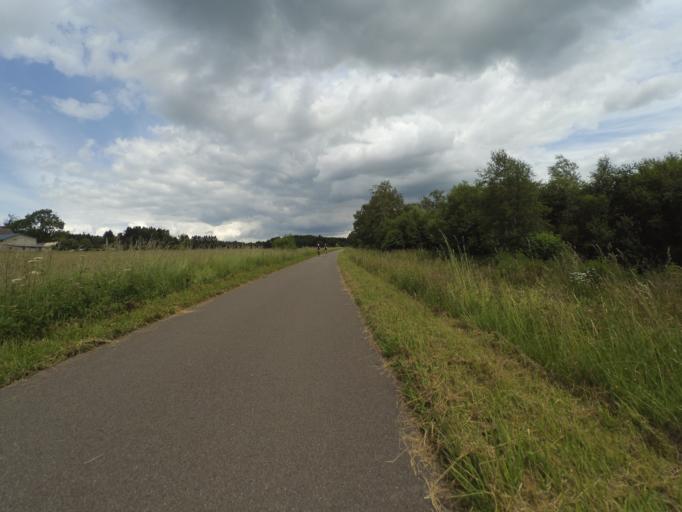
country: DE
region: North Rhine-Westphalia
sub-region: Regierungsbezirk Koln
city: Monschau
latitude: 50.5861
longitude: 6.2402
